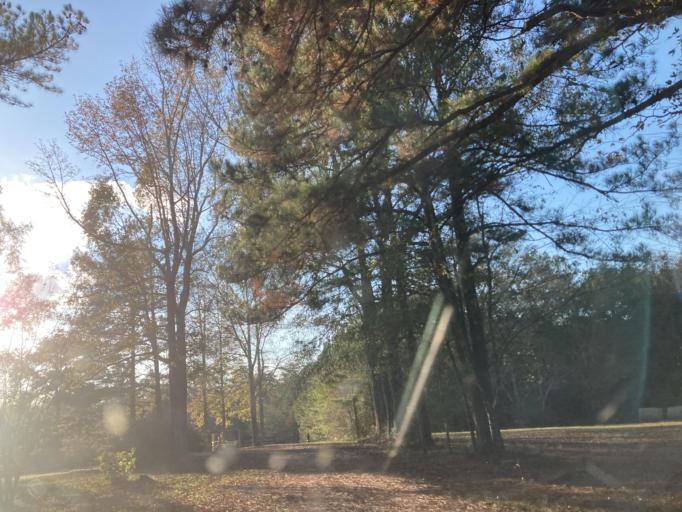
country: US
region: Mississippi
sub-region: Lamar County
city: Sumrall
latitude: 31.3973
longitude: -89.6264
